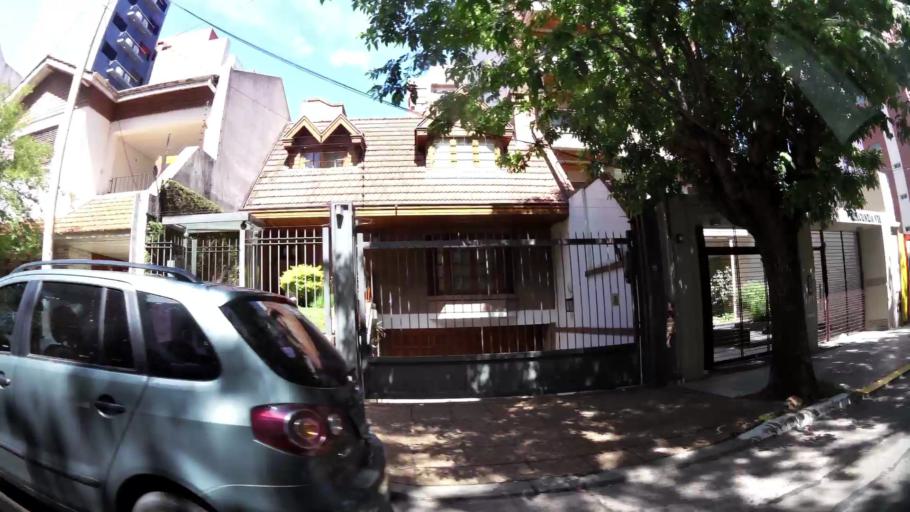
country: AR
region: Buenos Aires
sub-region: Partido de Quilmes
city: Quilmes
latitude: -34.7174
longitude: -58.2597
